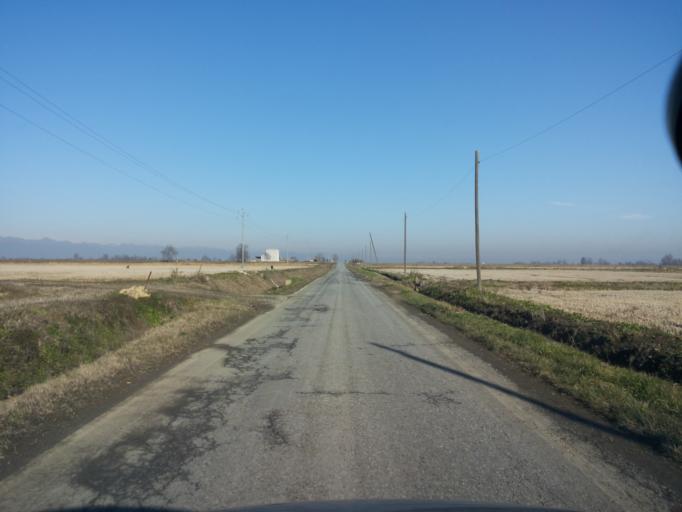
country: IT
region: Piedmont
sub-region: Provincia di Vercelli
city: Formigliana
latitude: 45.4143
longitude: 8.2493
